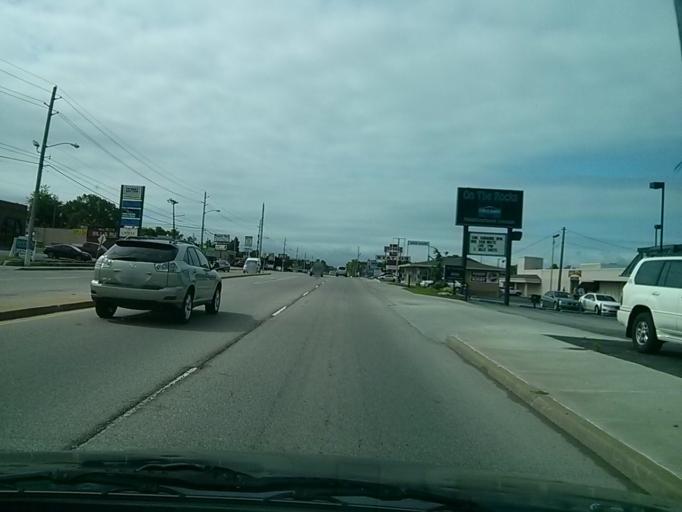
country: US
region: Oklahoma
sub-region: Tulsa County
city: Tulsa
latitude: 36.1182
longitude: -95.9225
